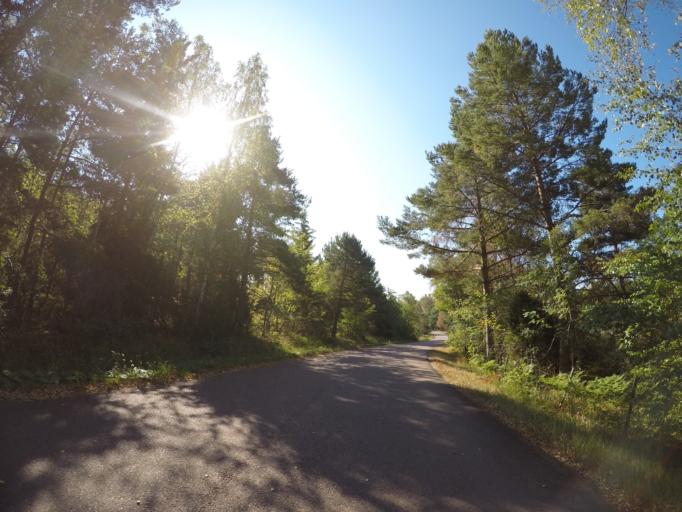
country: AX
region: Alands landsbygd
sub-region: Finstroem
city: Finstroem
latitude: 60.3296
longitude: 19.9123
